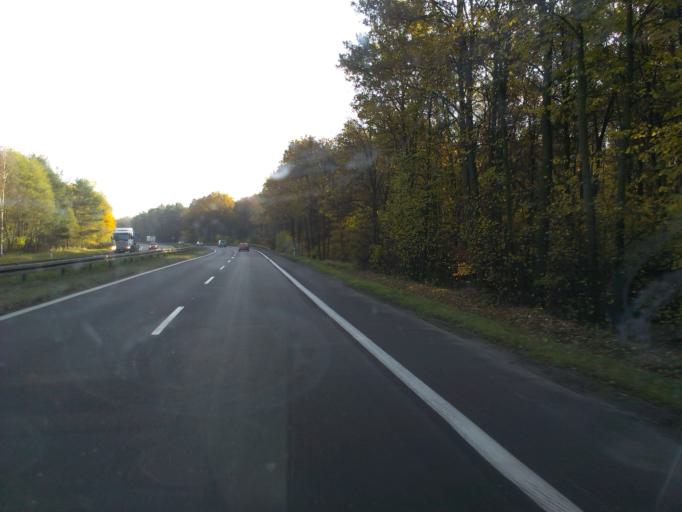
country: PL
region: Lower Silesian Voivodeship
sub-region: Powiat lubinski
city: Lubin
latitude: 51.4459
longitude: 16.1376
